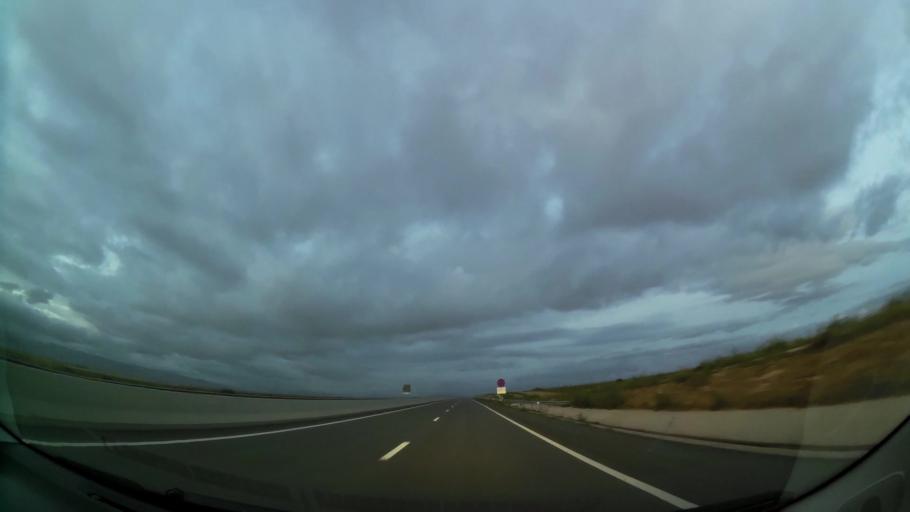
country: MA
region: Oriental
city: El Aioun
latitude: 34.6282
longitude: -2.3703
